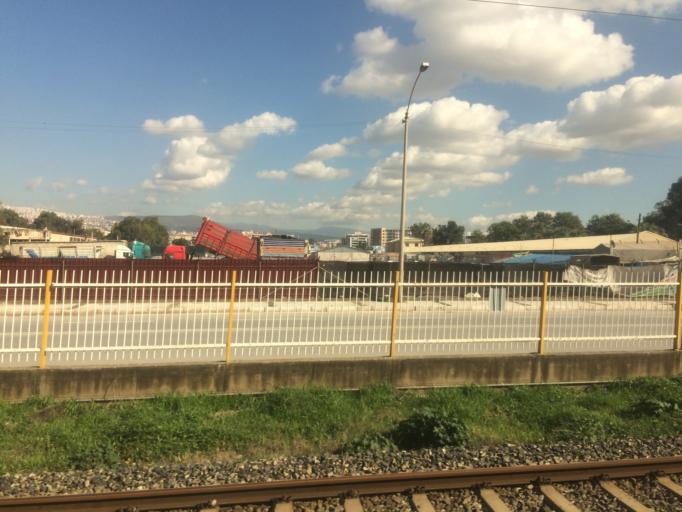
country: TR
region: Izmir
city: Izmir
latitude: 38.4587
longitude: 27.1680
